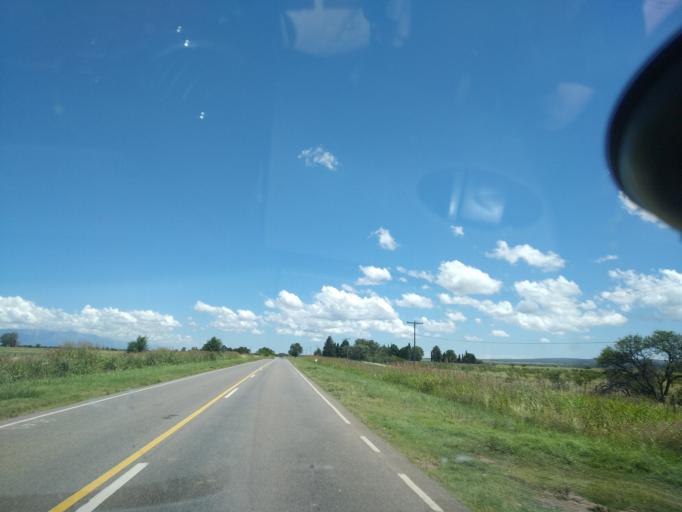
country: AR
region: Cordoba
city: Villa Cura Brochero
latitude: -31.5461
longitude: -65.1119
